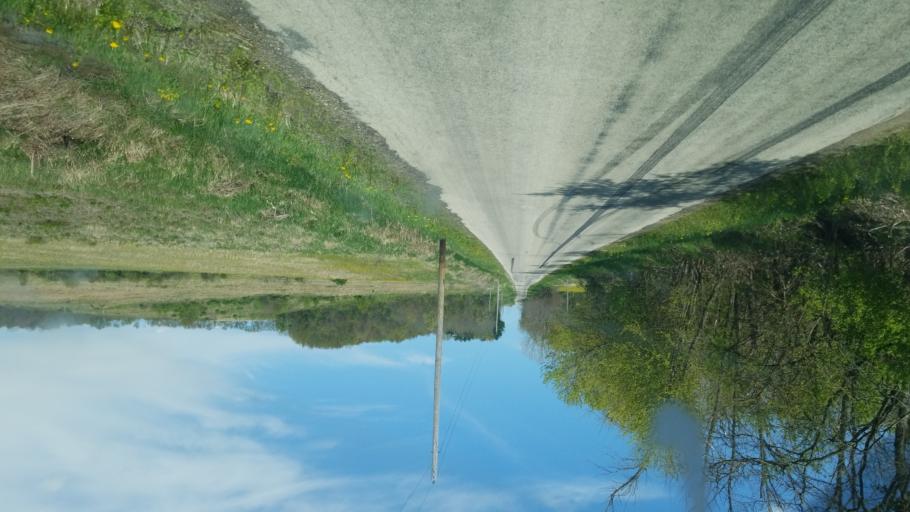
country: US
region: Ohio
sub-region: Wayne County
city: Shreve
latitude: 40.7670
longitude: -82.1173
